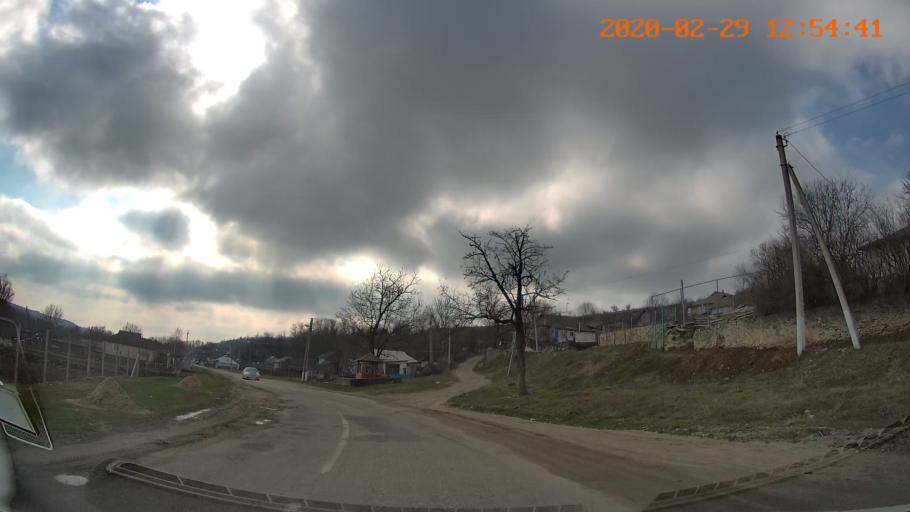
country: MD
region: Telenesti
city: Camenca
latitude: 48.1007
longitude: 28.7258
